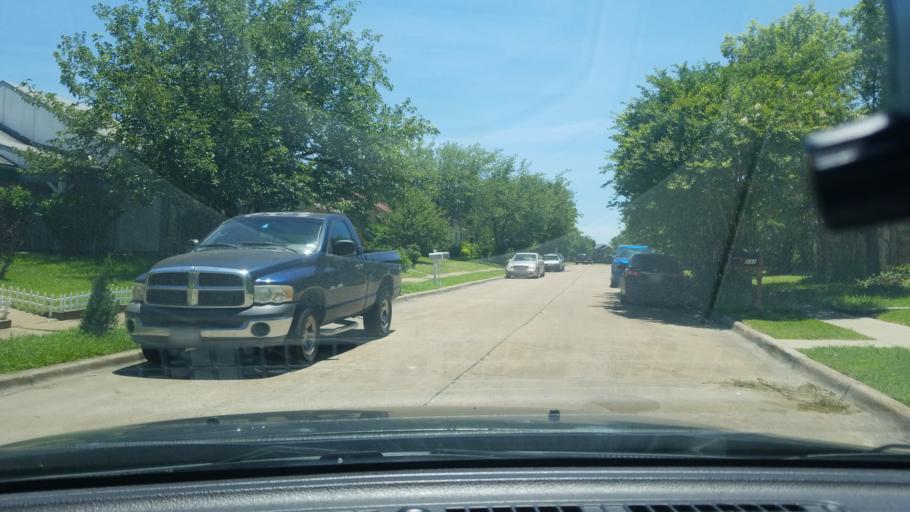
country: US
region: Texas
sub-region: Dallas County
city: Mesquite
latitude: 32.7745
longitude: -96.6061
